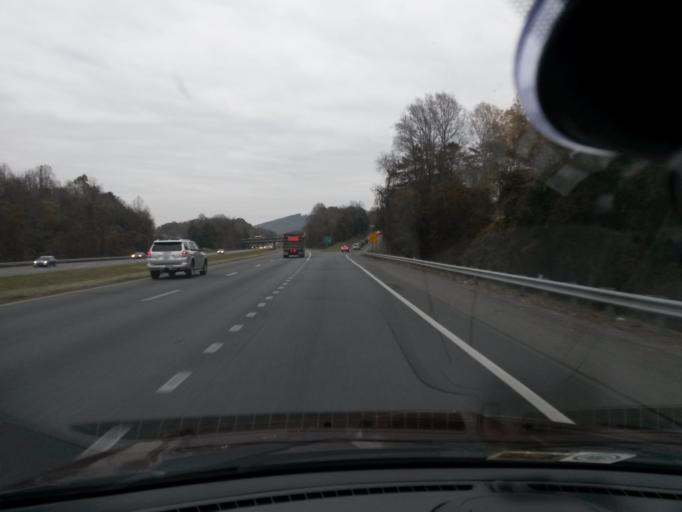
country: US
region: Virginia
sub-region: City of Charlottesville
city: Charlottesville
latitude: 38.0083
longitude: -78.5142
